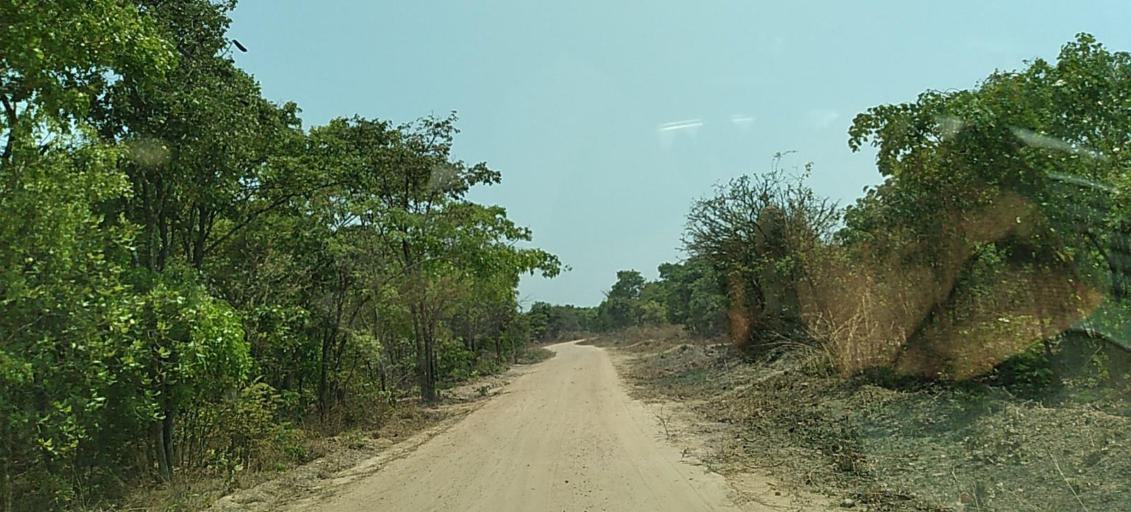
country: ZM
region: Copperbelt
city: Kalulushi
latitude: -12.9440
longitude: 28.1537
